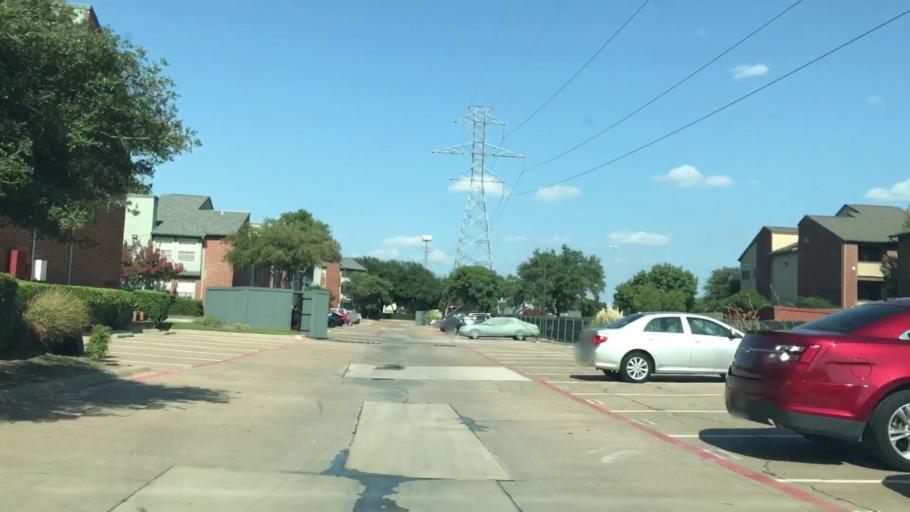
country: US
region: Texas
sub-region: Dallas County
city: Mesquite
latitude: 32.8182
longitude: -96.6338
